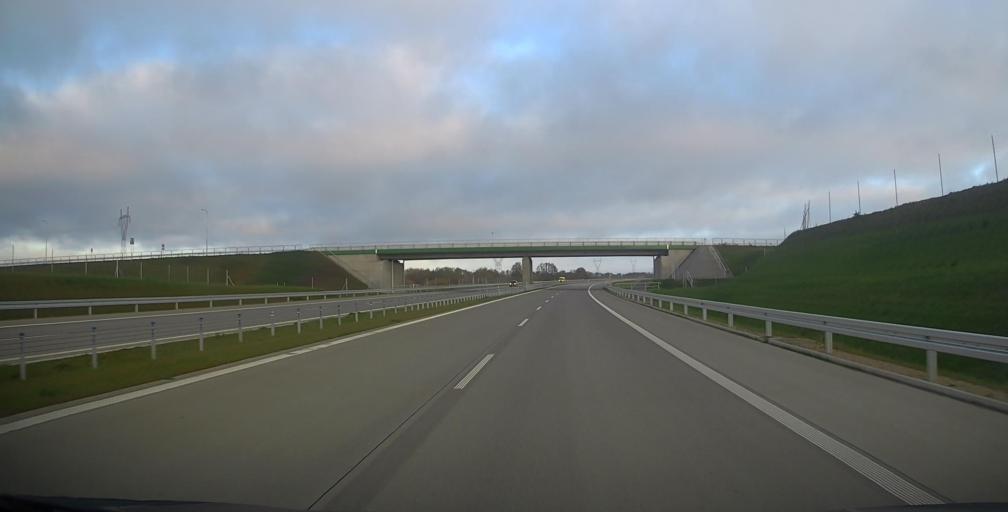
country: PL
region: Podlasie
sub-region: Powiat grajewski
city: Szczuczyn
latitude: 53.6361
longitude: 22.2923
